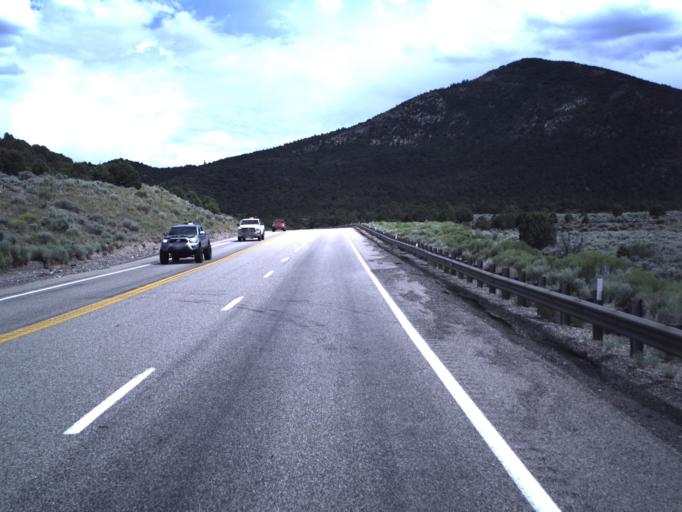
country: US
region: Utah
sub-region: Beaver County
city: Beaver
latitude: 38.0446
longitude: -112.5684
